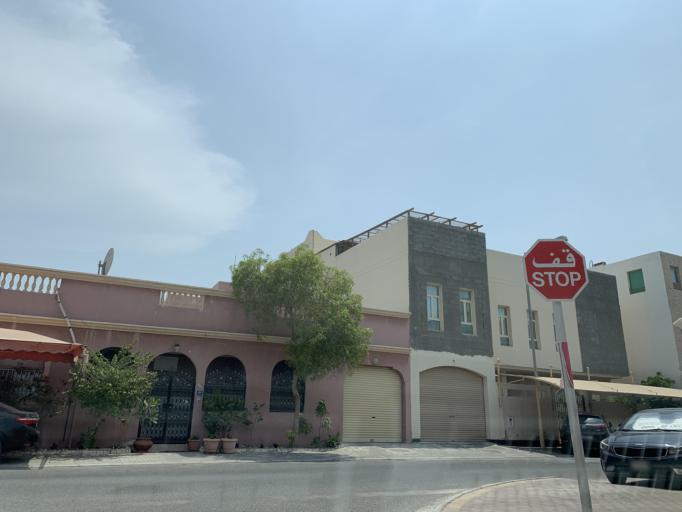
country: BH
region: Muharraq
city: Al Hadd
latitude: 26.2765
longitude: 50.6484
